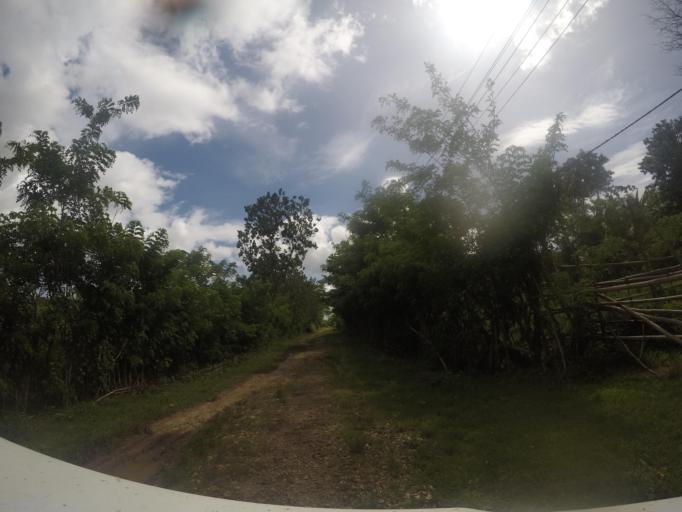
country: TL
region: Lautem
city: Lospalos
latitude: -8.4969
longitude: 127.0093
